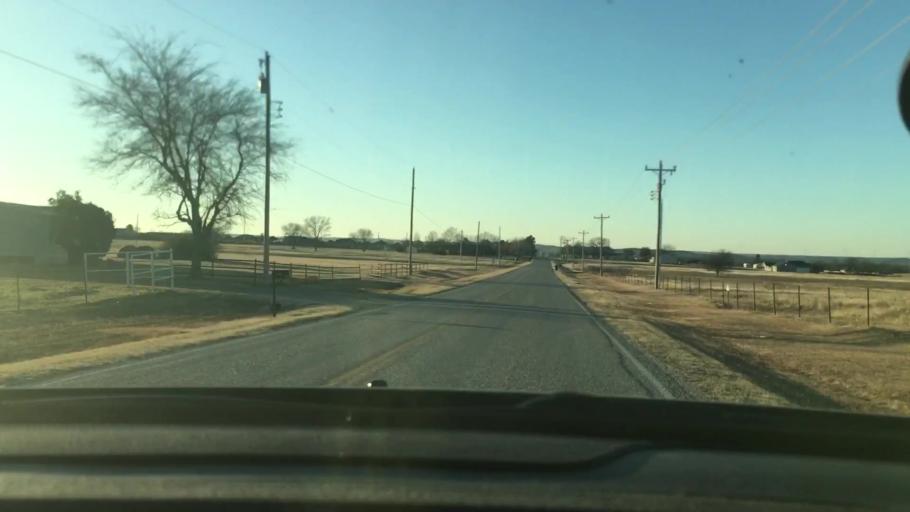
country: US
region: Oklahoma
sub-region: Murray County
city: Davis
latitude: 34.5027
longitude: -97.0904
